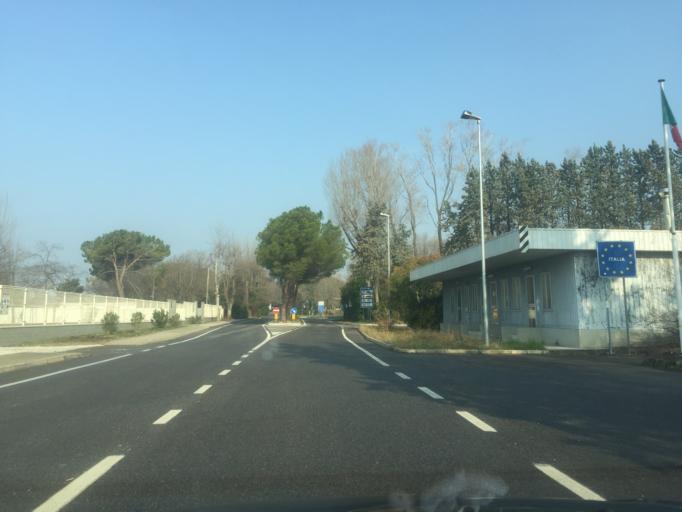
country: SI
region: Koper-Capodistria
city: Ankaran
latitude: 45.5947
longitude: 13.7241
